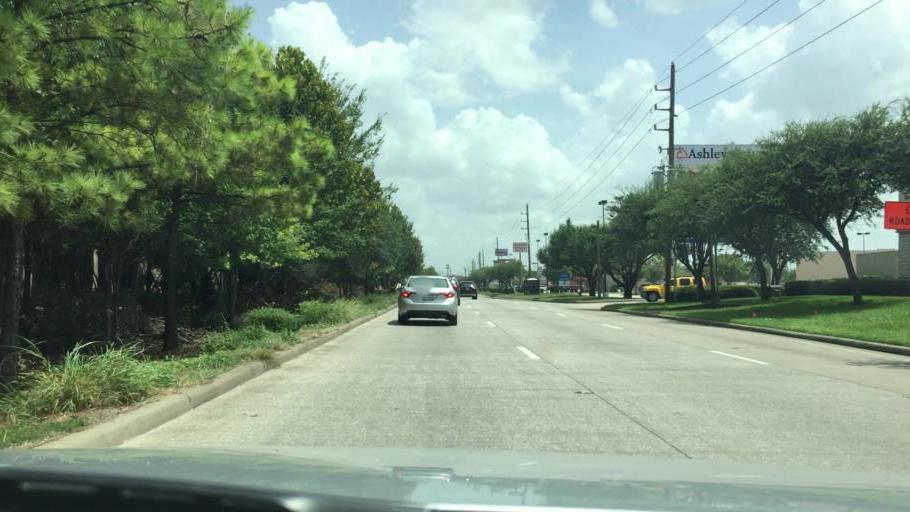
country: US
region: Texas
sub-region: Harris County
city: Hudson
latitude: 29.9598
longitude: -95.5469
